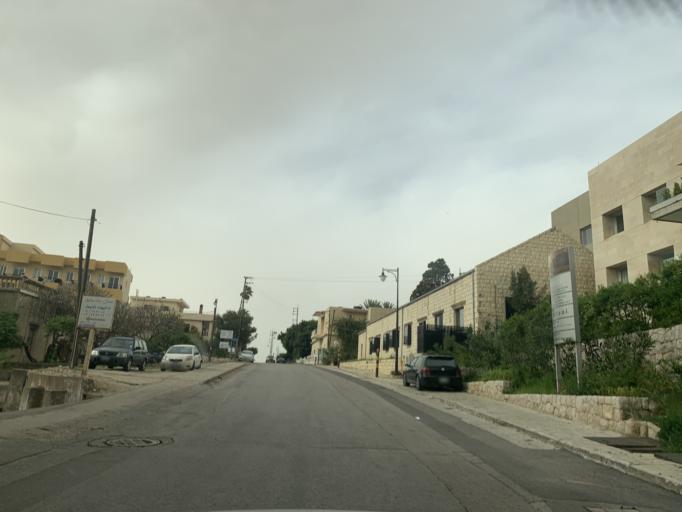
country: LB
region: Mont-Liban
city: Jbail
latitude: 34.0972
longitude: 35.6521
